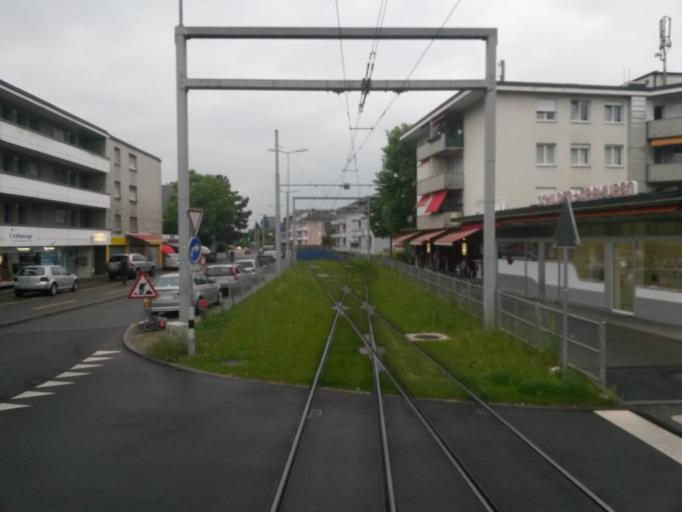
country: CH
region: Zurich
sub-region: Bezirk Zuerich
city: Zuerich (Kreis 12) / Schwamendingen-Mitte
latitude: 47.4050
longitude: 8.5713
